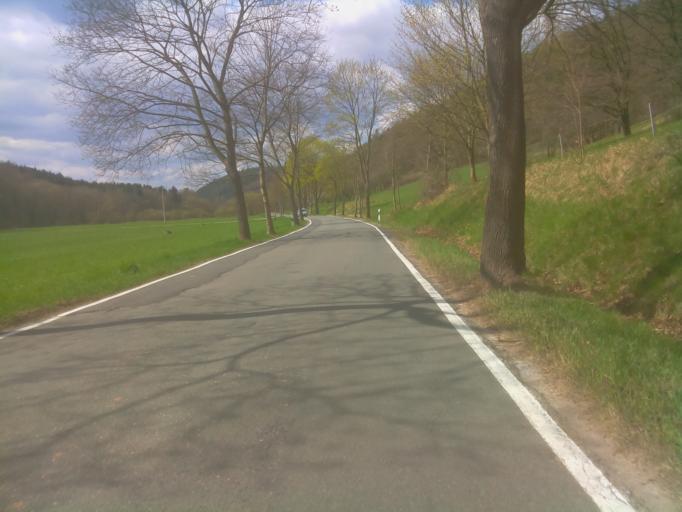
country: DE
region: Thuringia
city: Rattelsdorf
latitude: 50.8317
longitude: 11.7696
